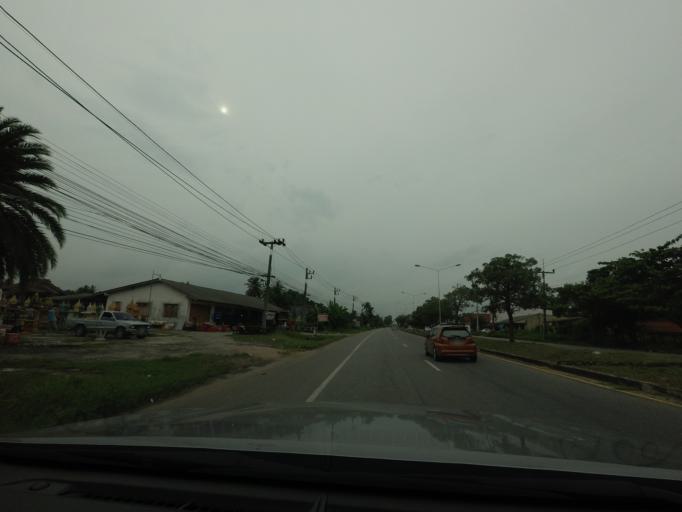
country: TH
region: Songkhla
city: Singhanakhon
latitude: 7.2586
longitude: 100.5265
